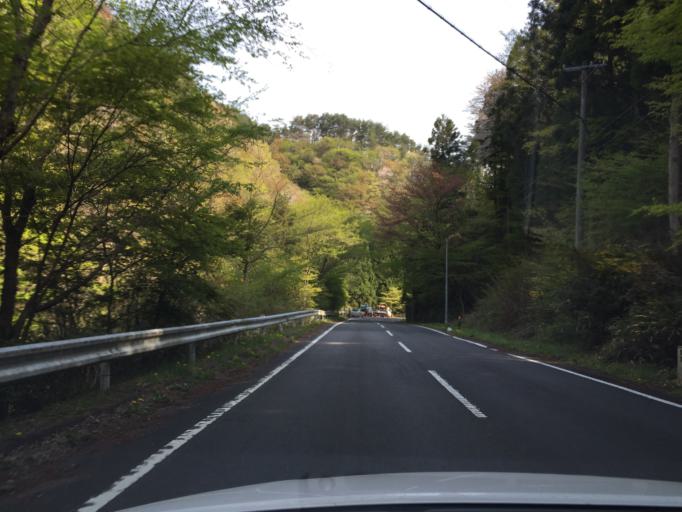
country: JP
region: Fukushima
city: Iwaki
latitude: 37.1749
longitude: 140.8509
